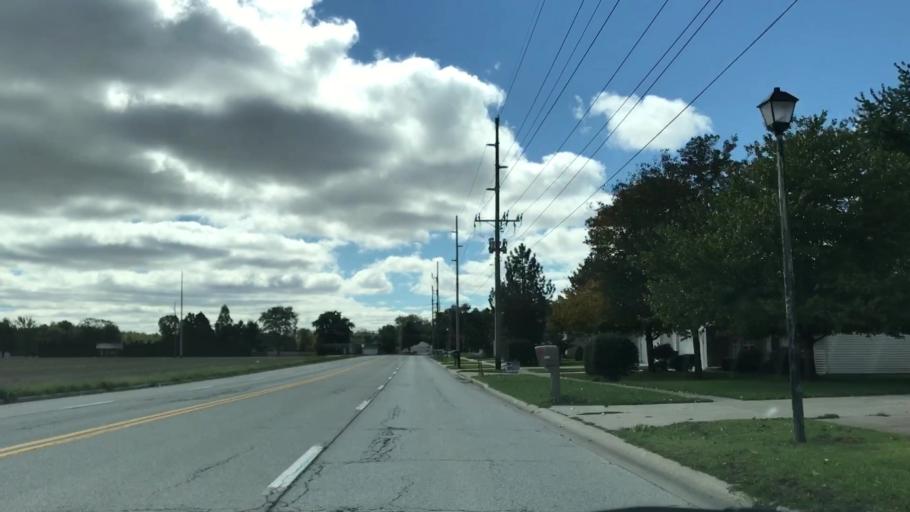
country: US
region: Indiana
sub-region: Howard County
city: Indian Heights
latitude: 40.4505
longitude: -86.0988
